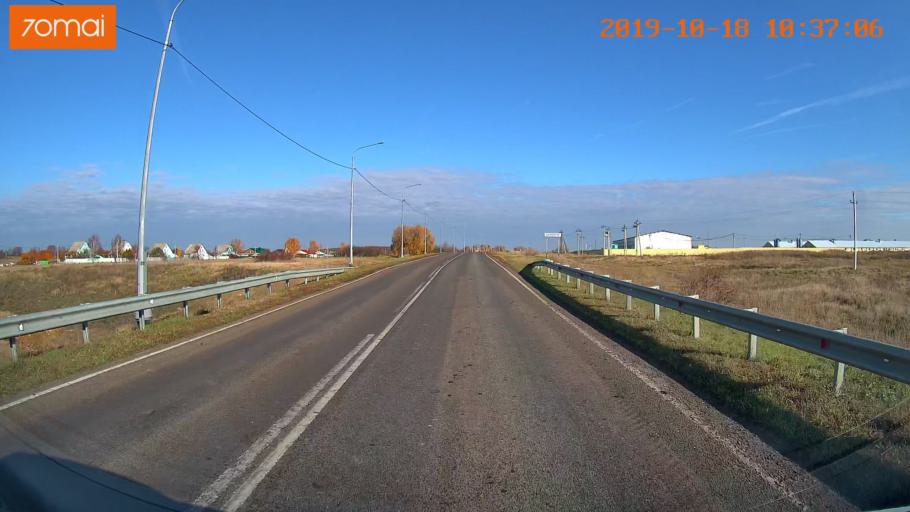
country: RU
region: Tula
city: Kurkino
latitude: 53.5583
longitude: 38.6296
